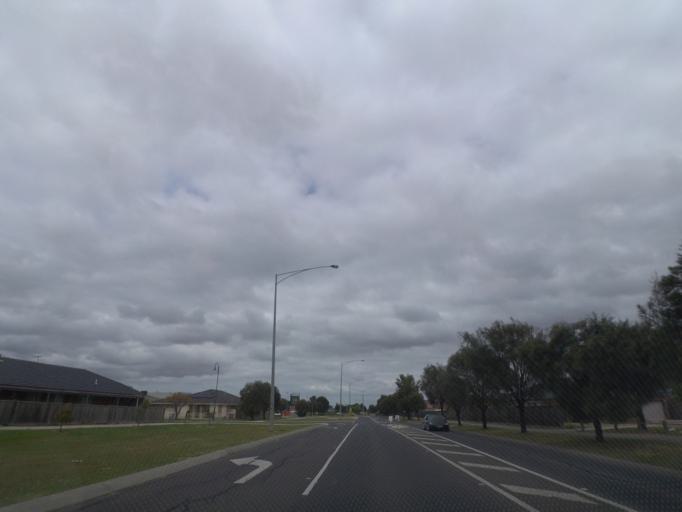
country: AU
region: Victoria
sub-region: Melton
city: Burnside Heights
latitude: -37.7216
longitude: 144.7507
